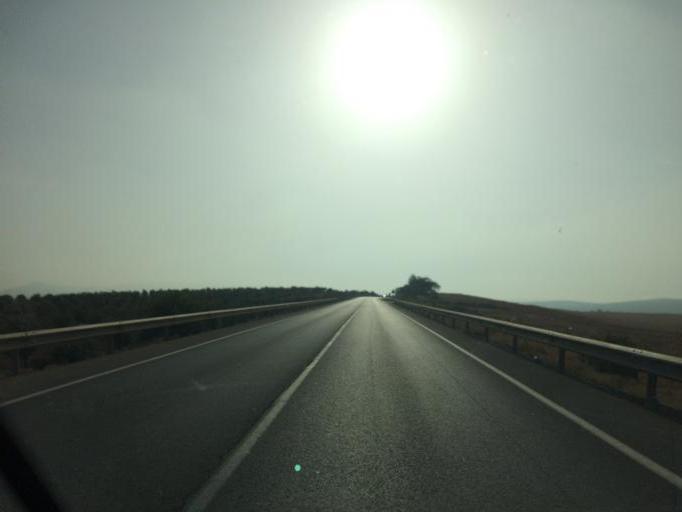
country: ES
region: Andalusia
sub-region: Provincia de Malaga
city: Campillos
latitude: 37.0526
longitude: -4.7860
